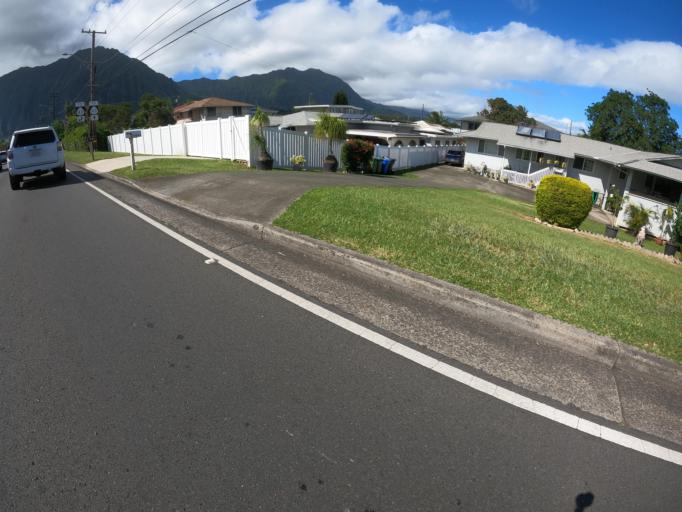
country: US
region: Hawaii
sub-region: Honolulu County
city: Kane'ohe
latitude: 21.4038
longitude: -157.7970
